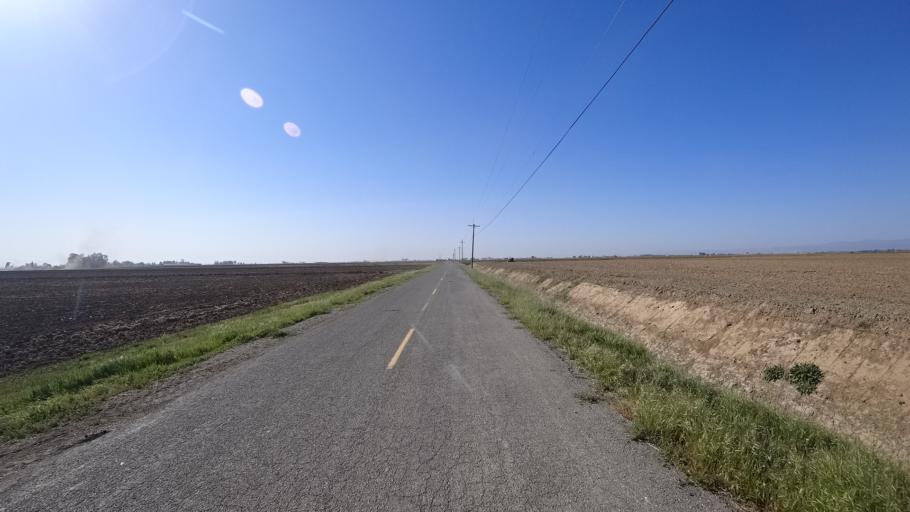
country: US
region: California
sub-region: Glenn County
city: Willows
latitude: 39.5630
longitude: -122.1171
